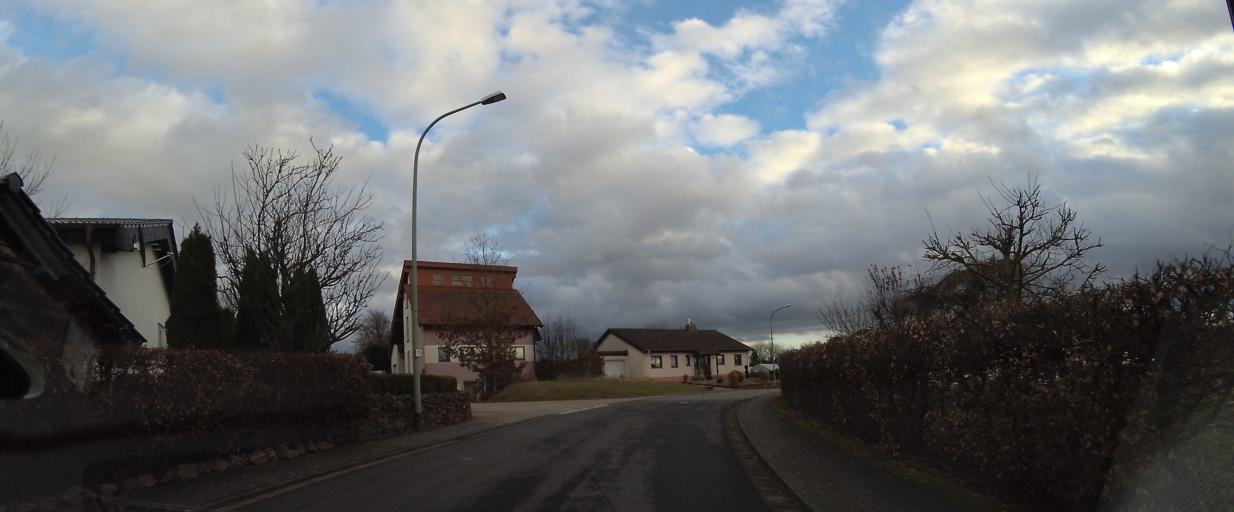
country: DE
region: Saarland
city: Schiffweiler
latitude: 49.3760
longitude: 7.0942
